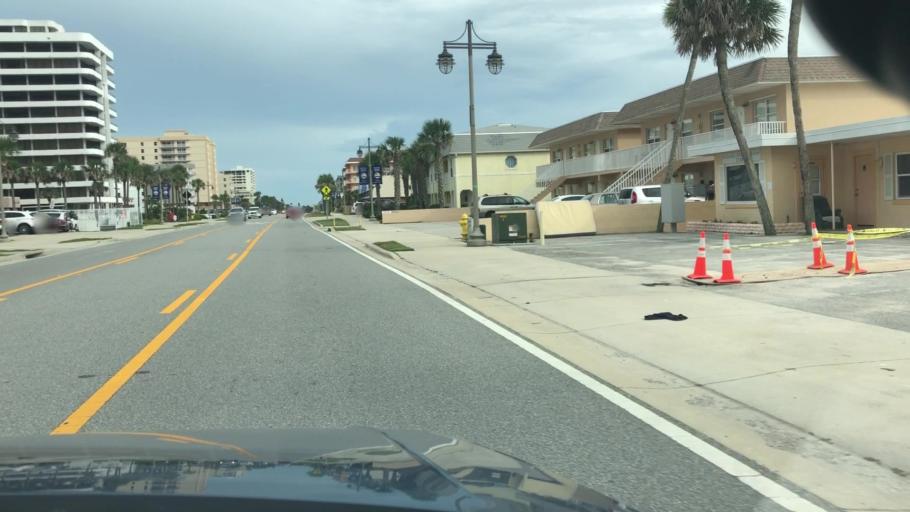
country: US
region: Florida
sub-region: Volusia County
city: Port Orange
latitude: 29.1447
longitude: -80.9657
